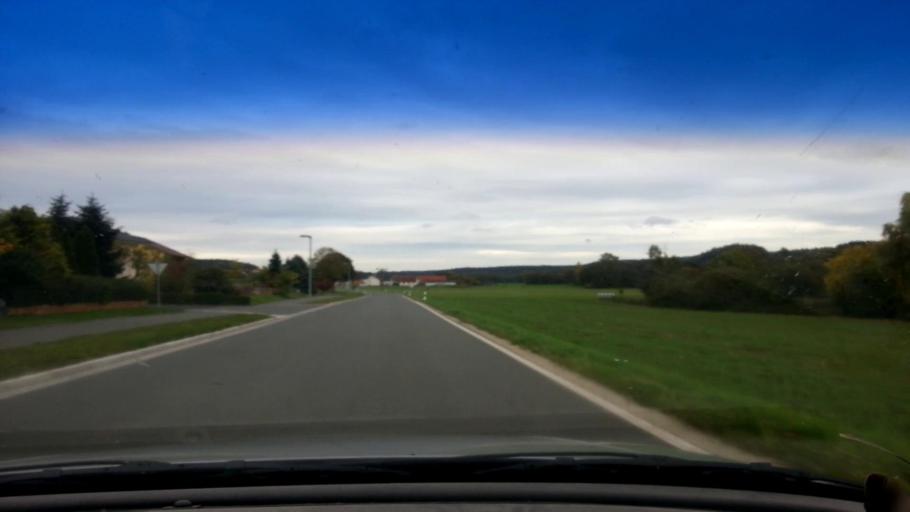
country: DE
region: Bavaria
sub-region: Upper Franconia
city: Burgwindheim
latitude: 49.8725
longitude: 10.6292
